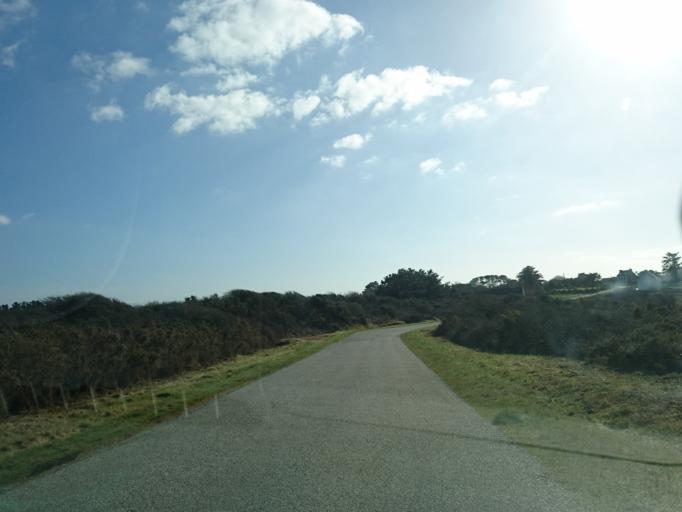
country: FR
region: Brittany
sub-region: Departement du Finistere
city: Roscanvel
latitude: 48.3275
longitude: -4.5690
